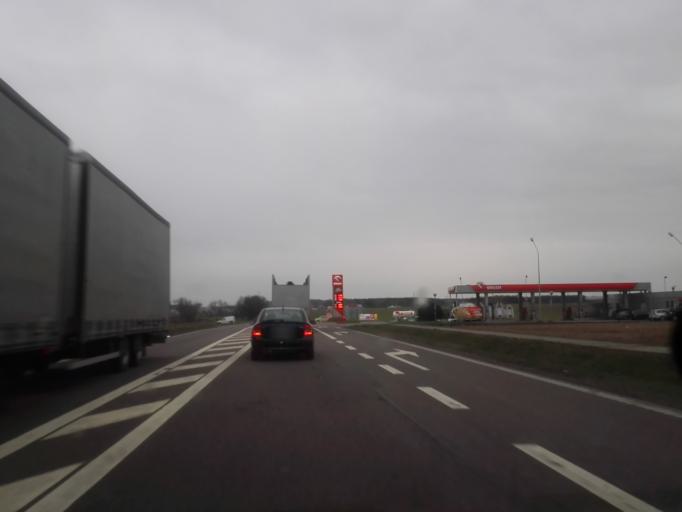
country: PL
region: Podlasie
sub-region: Powiat grajewski
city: Grajewo
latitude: 53.6296
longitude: 22.4158
